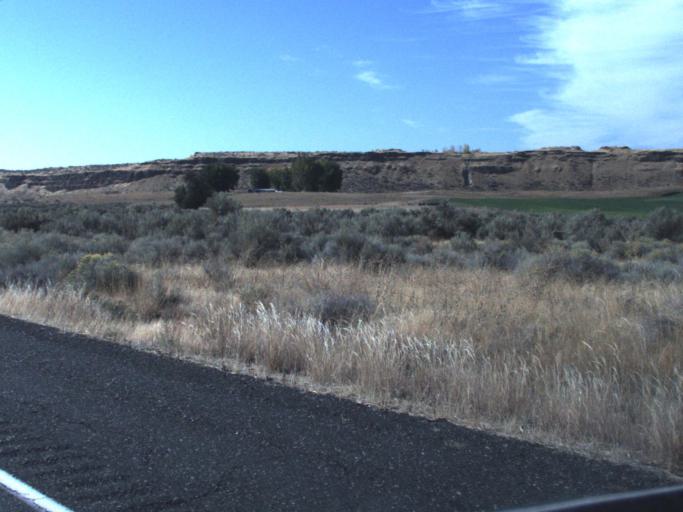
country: US
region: Washington
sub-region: Franklin County
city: Basin City
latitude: 46.4778
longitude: -119.0112
